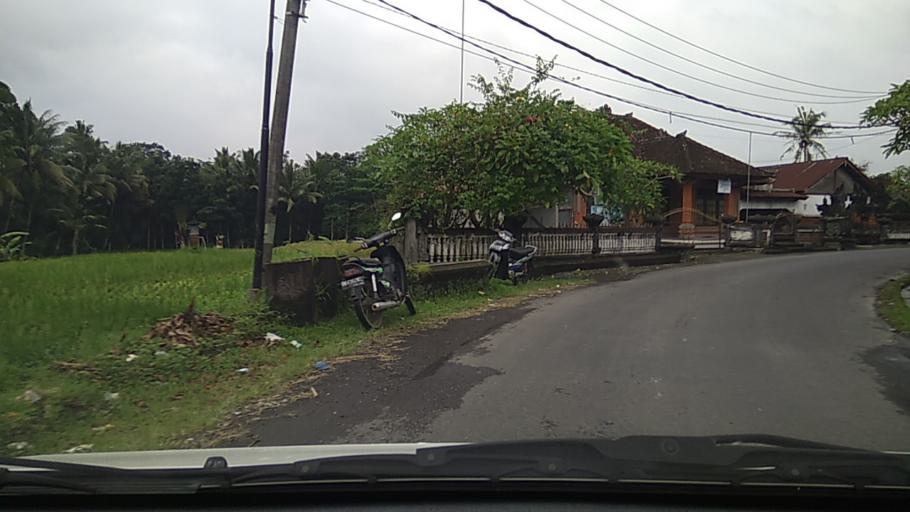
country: ID
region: Bali
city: Banjar Dujung Kaja
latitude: -8.4150
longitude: 115.2951
